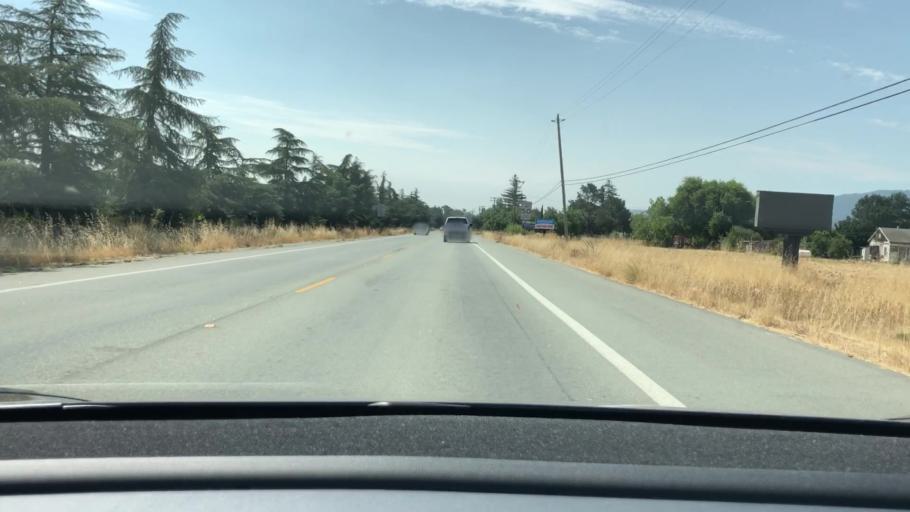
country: US
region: California
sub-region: Santa Clara County
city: San Martin
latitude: 37.0467
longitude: -121.6018
